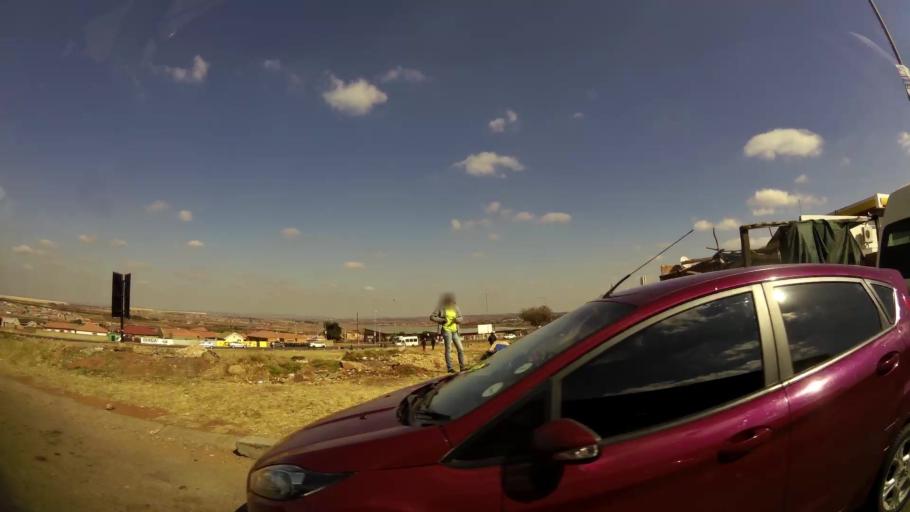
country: ZA
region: Gauteng
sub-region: West Rand District Municipality
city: Randfontein
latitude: -26.1668
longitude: 27.7796
